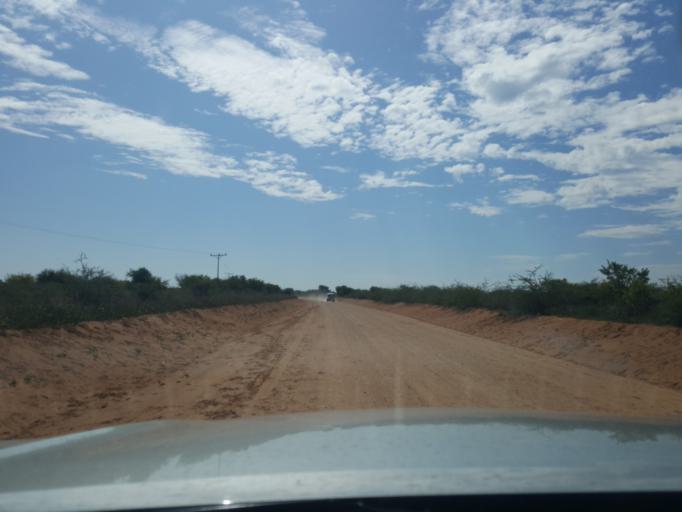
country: BW
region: Kweneng
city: Khudumelapye
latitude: -23.8509
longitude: 24.8719
